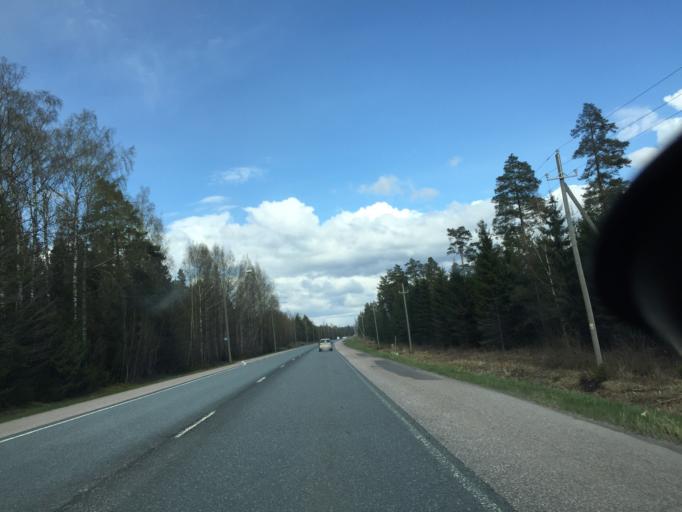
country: FI
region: Uusimaa
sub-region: Raaseporin
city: Ekenaes
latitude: 59.9983
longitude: 23.5119
